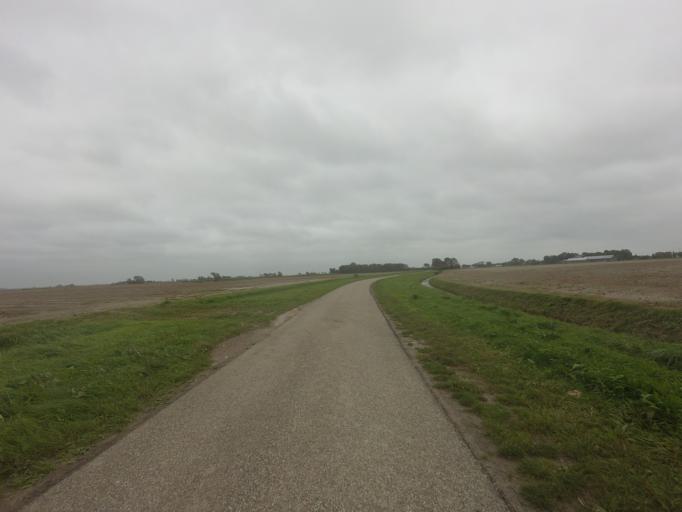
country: NL
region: Friesland
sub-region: Gemeente Ferwerderadiel
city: Ferwert
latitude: 53.3429
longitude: 5.8576
